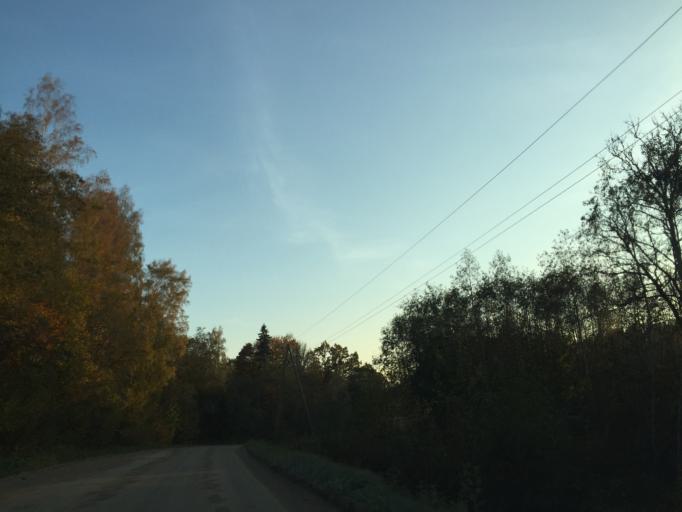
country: LV
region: Vainode
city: Vainode
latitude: 56.5051
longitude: 21.8241
